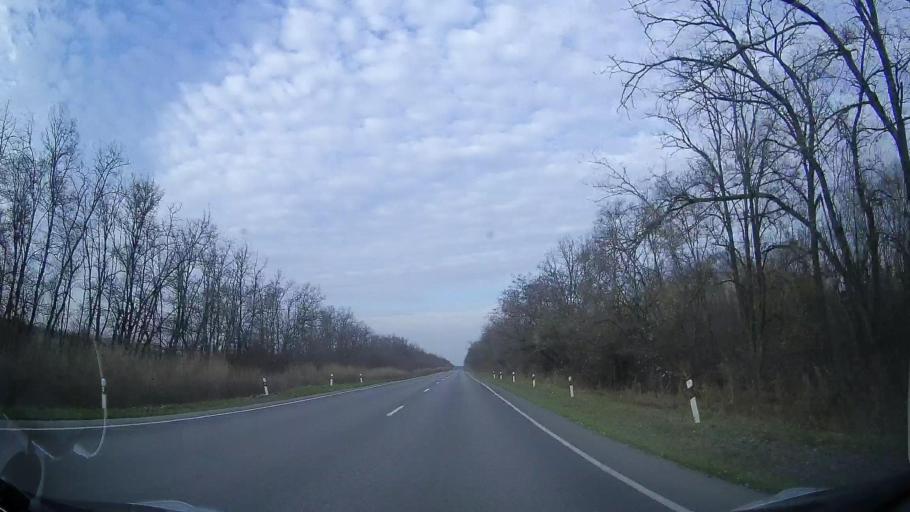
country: RU
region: Rostov
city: Bagayevskaya
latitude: 47.1174
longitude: 40.2767
